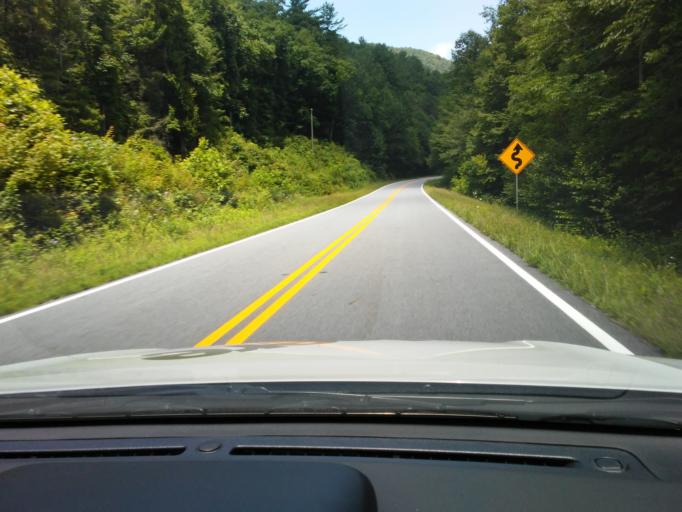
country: US
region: Georgia
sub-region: Towns County
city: Hiawassee
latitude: 34.8534
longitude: -83.7932
